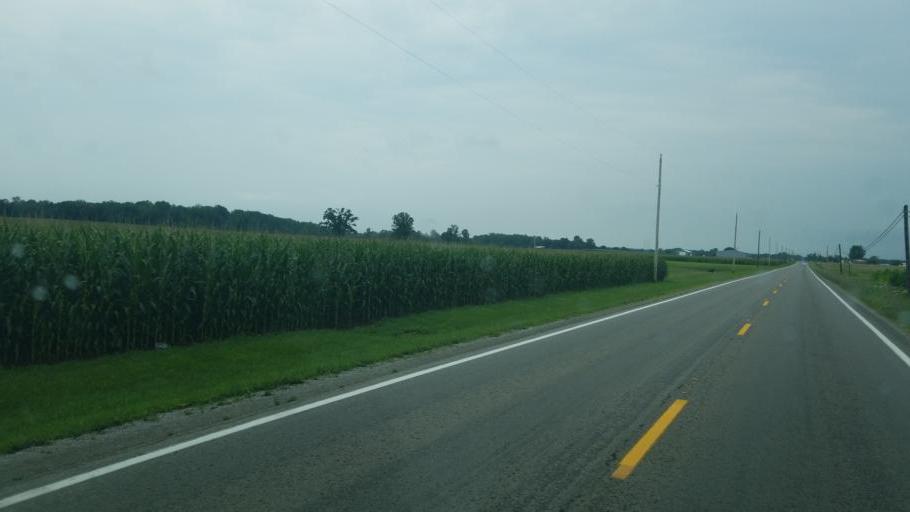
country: US
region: Ohio
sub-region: Hardin County
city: Kenton
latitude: 40.6352
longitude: -83.6239
